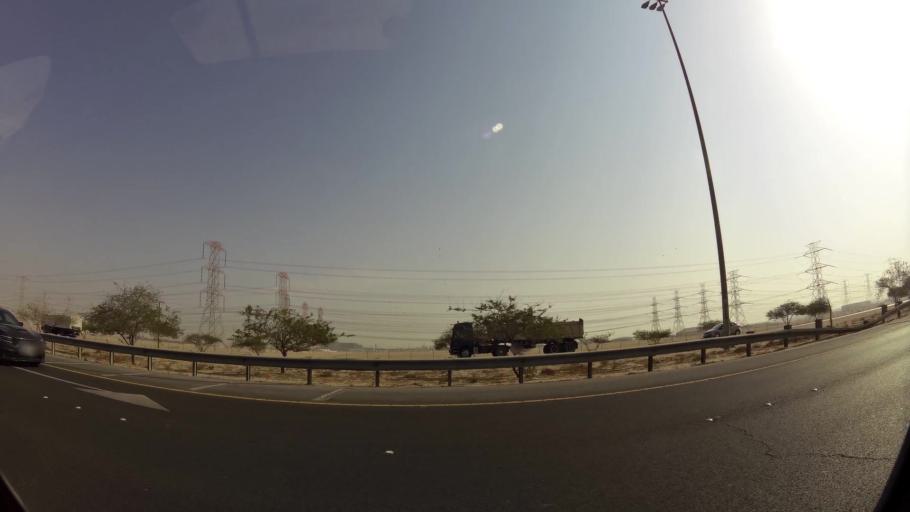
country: KW
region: Al Ahmadi
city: Al Ahmadi
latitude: 28.9763
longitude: 48.1102
